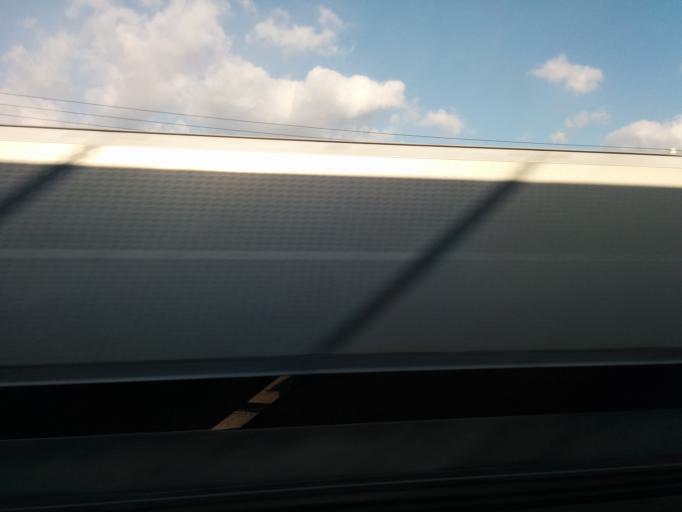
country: JP
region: Shizuoka
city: Fujieda
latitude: 34.8579
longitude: 138.2862
